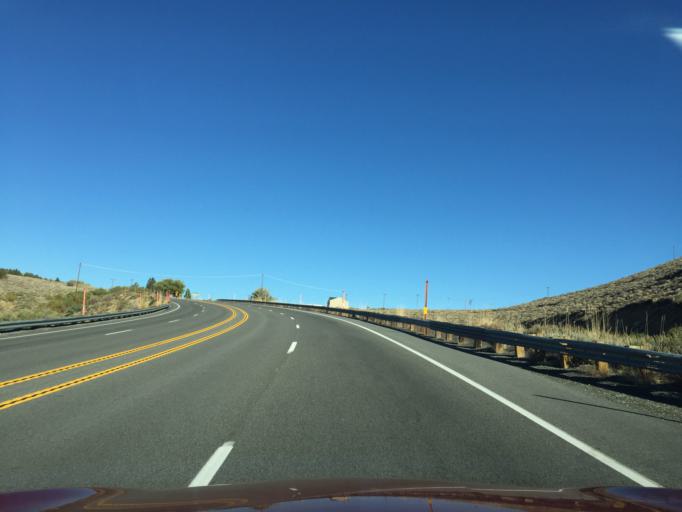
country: US
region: California
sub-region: Mono County
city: Bridgeport
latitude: 38.0839
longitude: -119.1783
